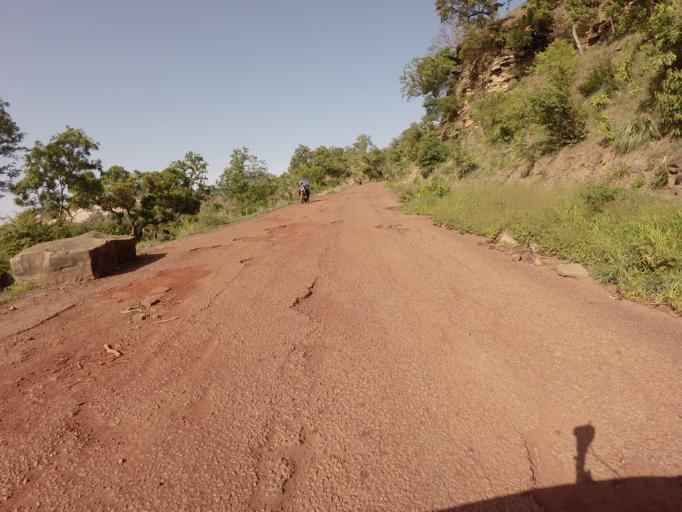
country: GH
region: Upper East
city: Bawku
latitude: 10.6420
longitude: -0.1932
